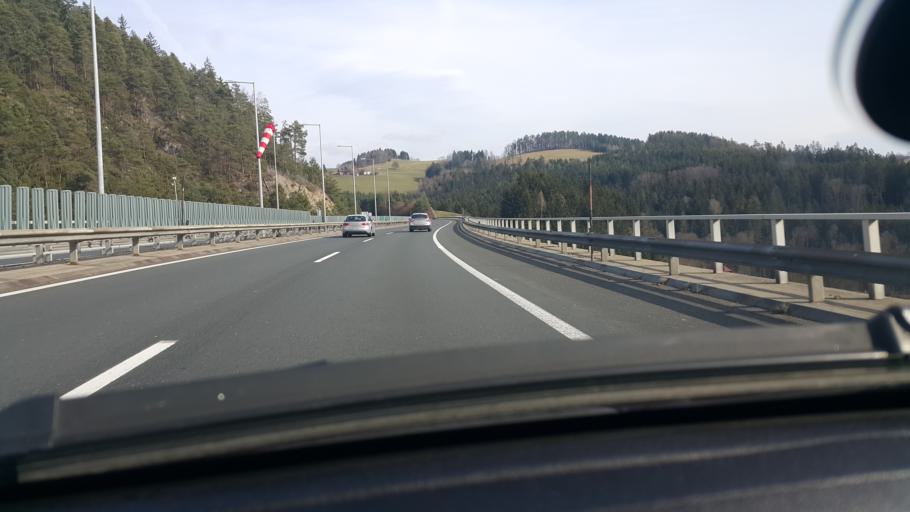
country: AT
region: Carinthia
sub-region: Politischer Bezirk Volkermarkt
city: Griffen
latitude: 46.7006
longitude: 14.7604
